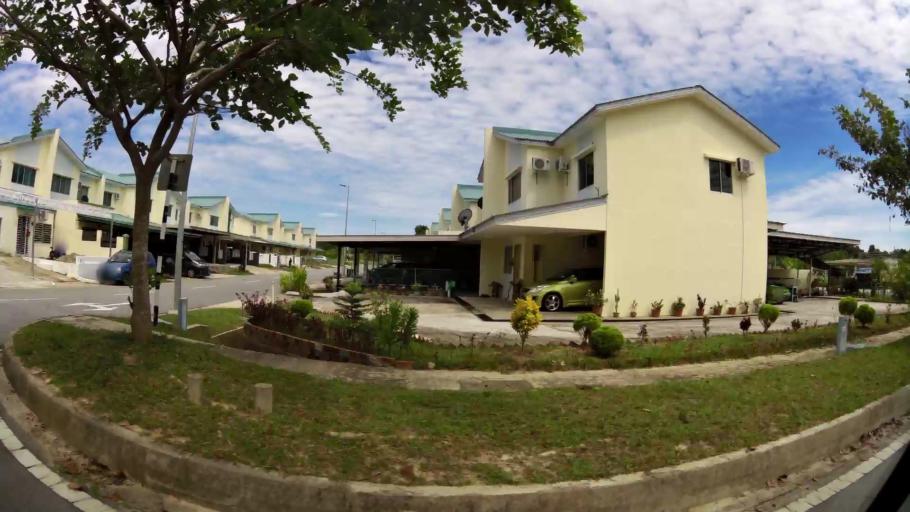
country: BN
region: Brunei and Muara
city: Bandar Seri Begawan
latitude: 4.9869
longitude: 115.0181
